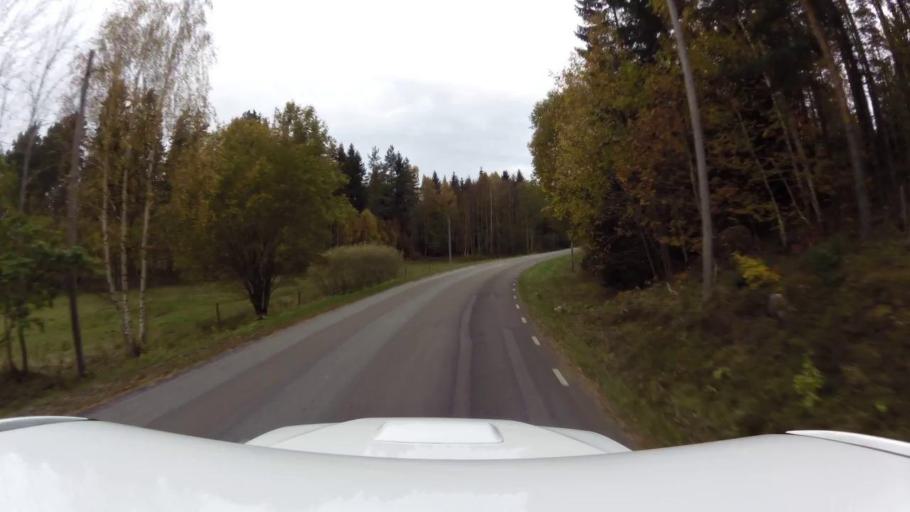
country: SE
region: OEstergoetland
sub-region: Linkopings Kommun
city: Ljungsbro
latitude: 58.5508
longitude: 15.4119
